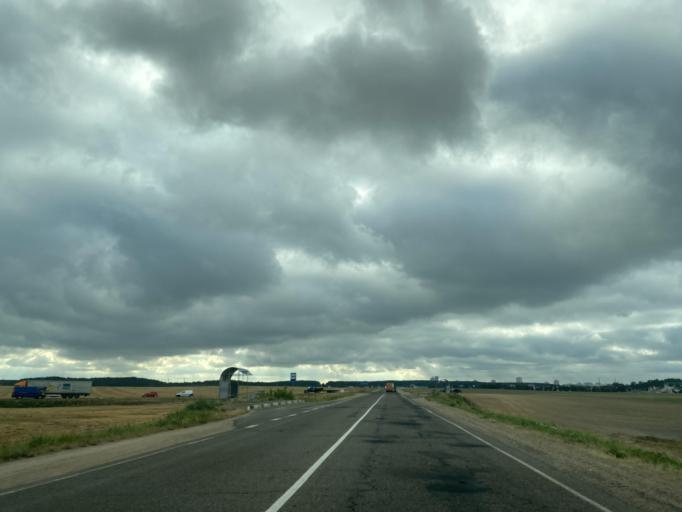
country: BY
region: Minsk
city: Bal'shavik
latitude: 53.9796
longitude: 27.5753
